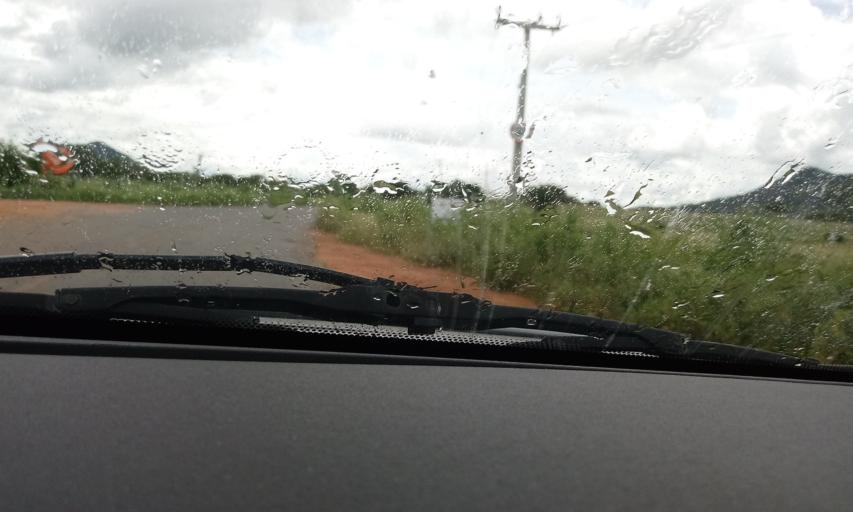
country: BR
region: Bahia
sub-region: Guanambi
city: Guanambi
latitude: -14.0952
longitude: -42.8725
